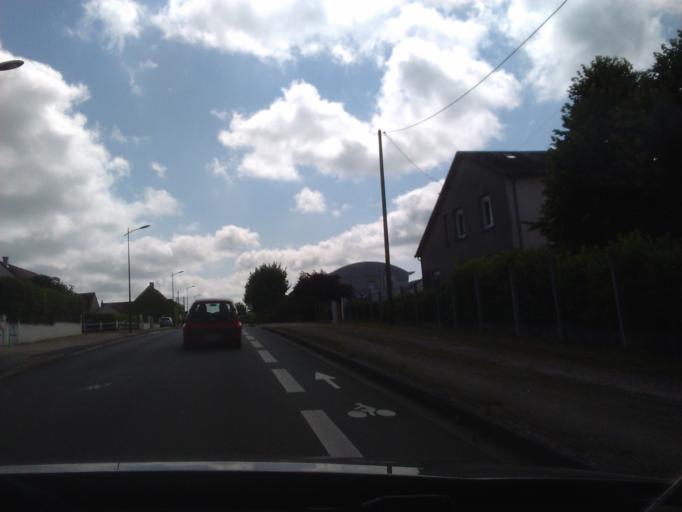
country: FR
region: Centre
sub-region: Departement du Loir-et-Cher
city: Vendome
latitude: 47.7824
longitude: 1.0653
